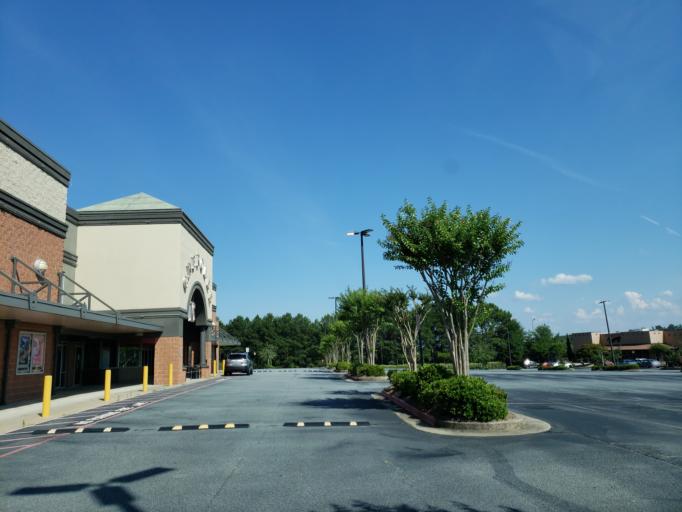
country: US
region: Georgia
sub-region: Cherokee County
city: Woodstock
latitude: 34.1077
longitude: -84.5435
